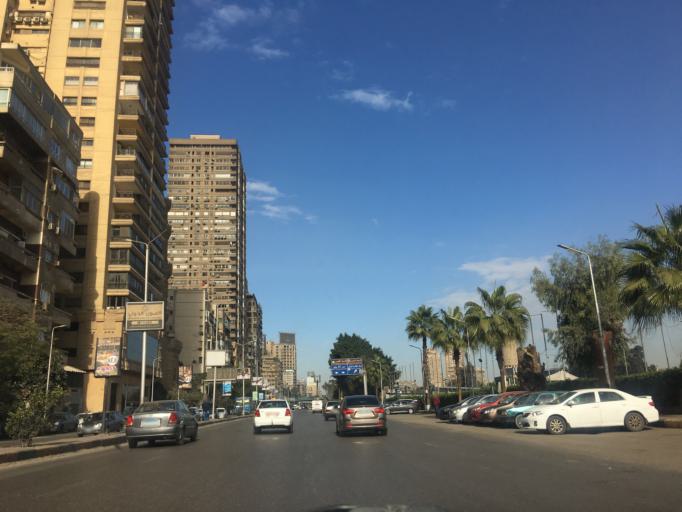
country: EG
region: Muhafazat al Qahirah
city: Cairo
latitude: 30.0445
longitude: 31.2189
